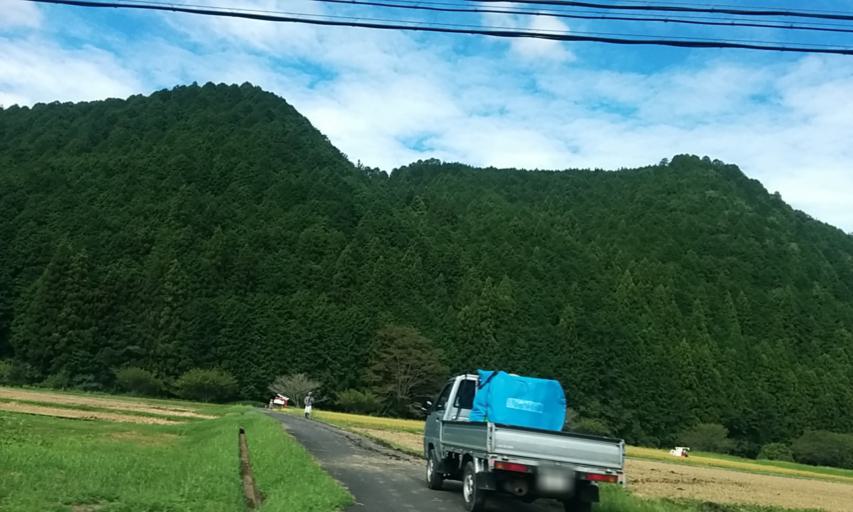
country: JP
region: Gifu
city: Minokamo
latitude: 35.5699
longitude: 137.0840
